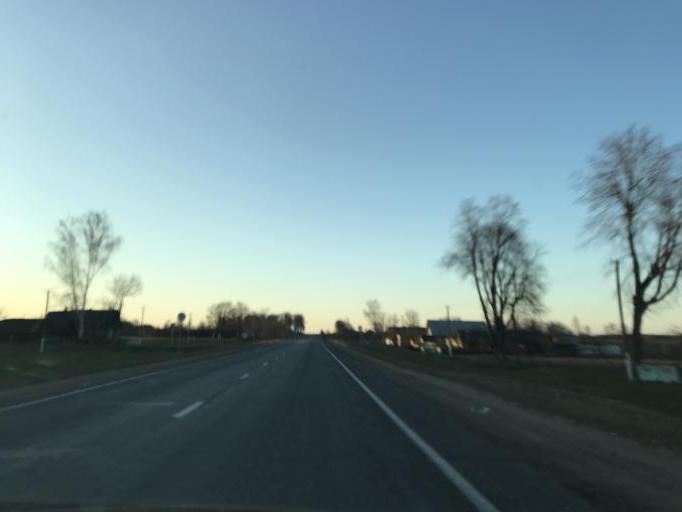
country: BY
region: Gomel
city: Dowsk
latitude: 53.1054
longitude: 30.5013
